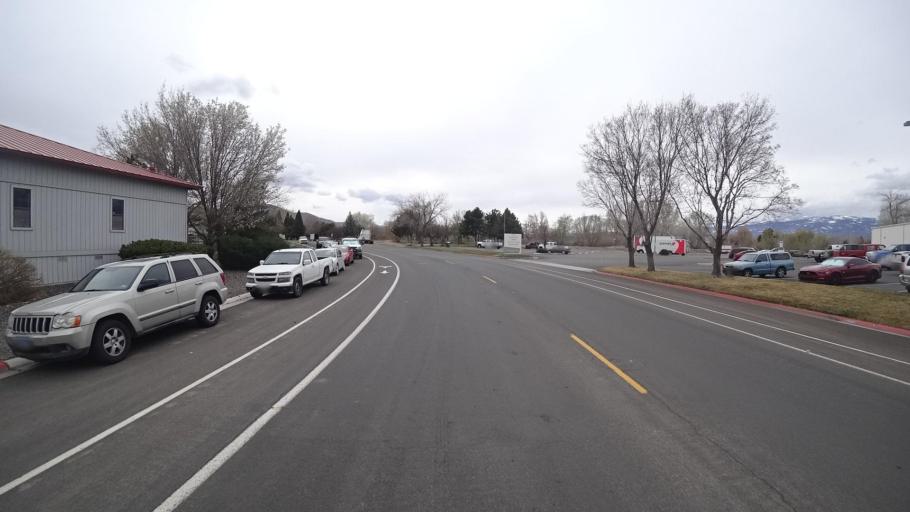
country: US
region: Nevada
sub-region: Washoe County
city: Sparks
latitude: 39.5154
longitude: -119.7344
